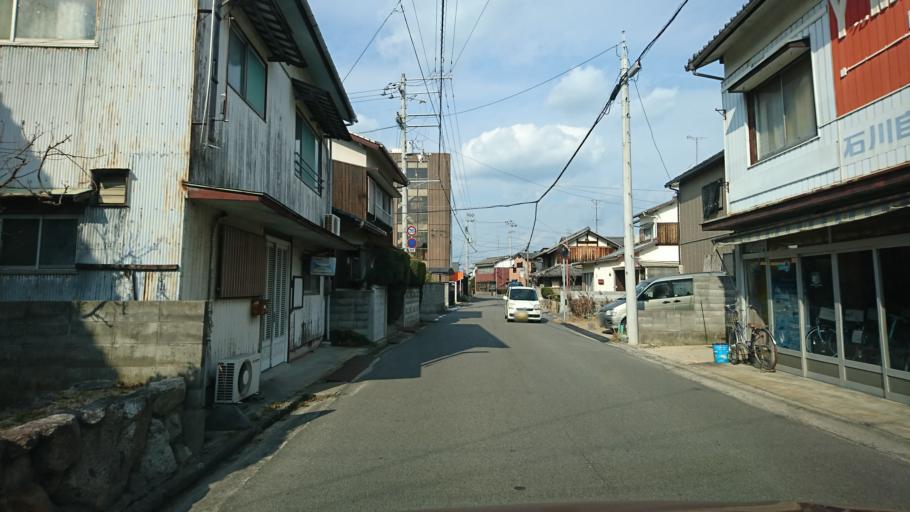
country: JP
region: Ehime
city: Saijo
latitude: 34.0223
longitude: 133.0392
